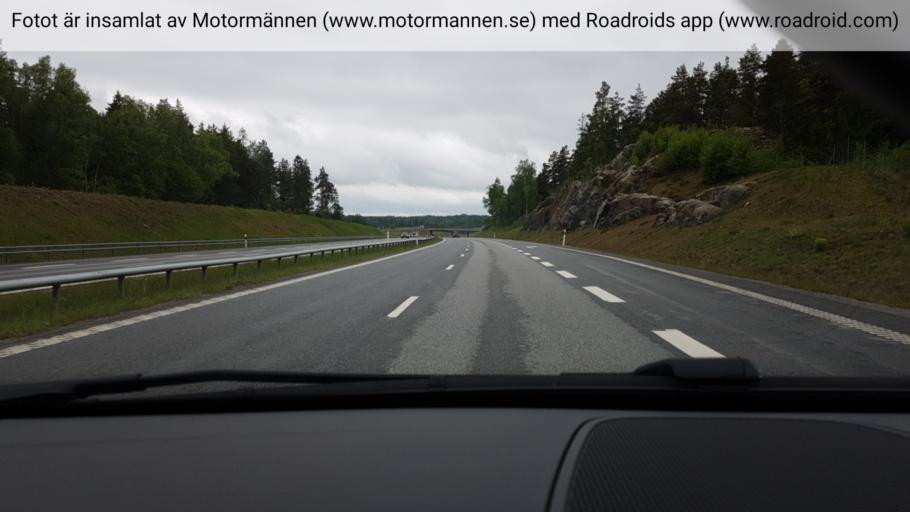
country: SE
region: Stockholm
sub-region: Haninge Kommun
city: Jordbro
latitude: 59.0735
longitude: 18.0690
